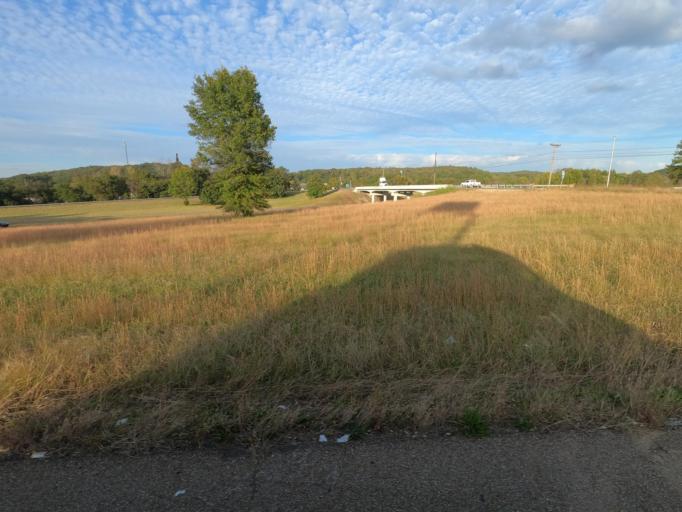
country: US
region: Tennessee
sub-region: Humphreys County
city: Waverly
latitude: 35.8791
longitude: -87.8027
